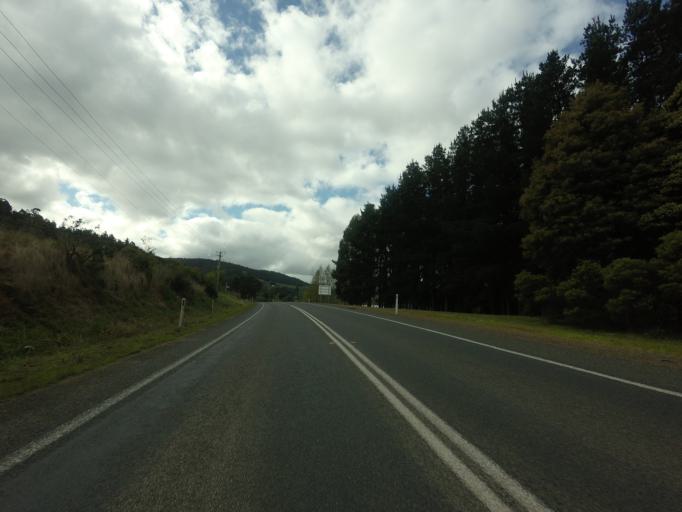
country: AU
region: Tasmania
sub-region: Huon Valley
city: Franklin
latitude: -43.1250
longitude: 146.9896
